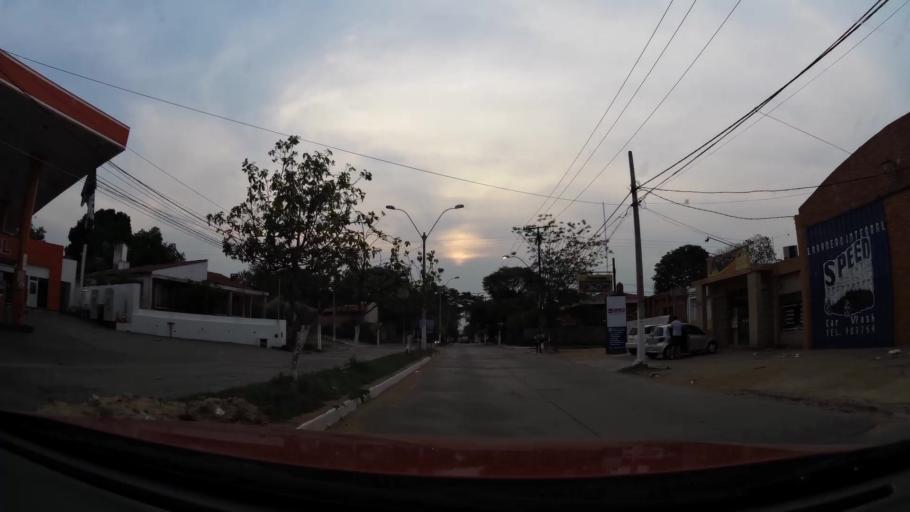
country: PY
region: Central
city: Lambare
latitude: -25.3424
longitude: -57.6317
